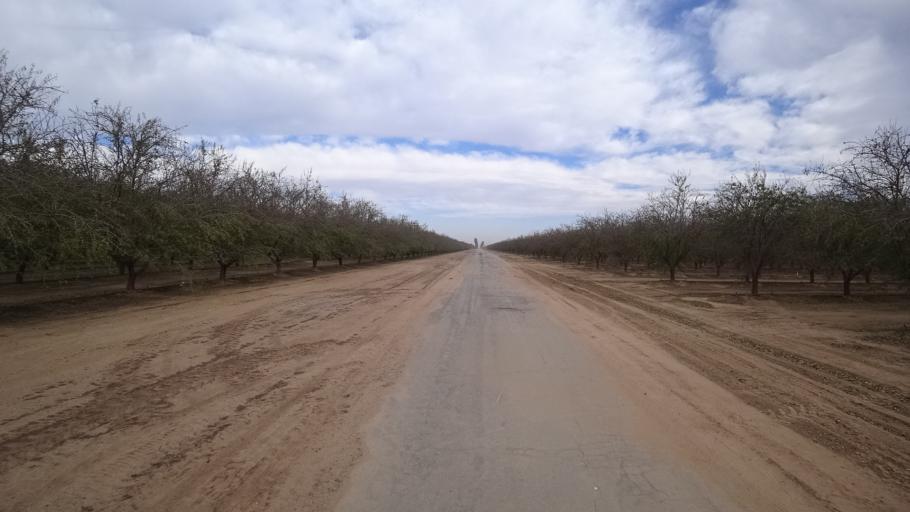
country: US
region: California
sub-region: Kern County
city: Rosedale
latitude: 35.4226
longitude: -119.1722
